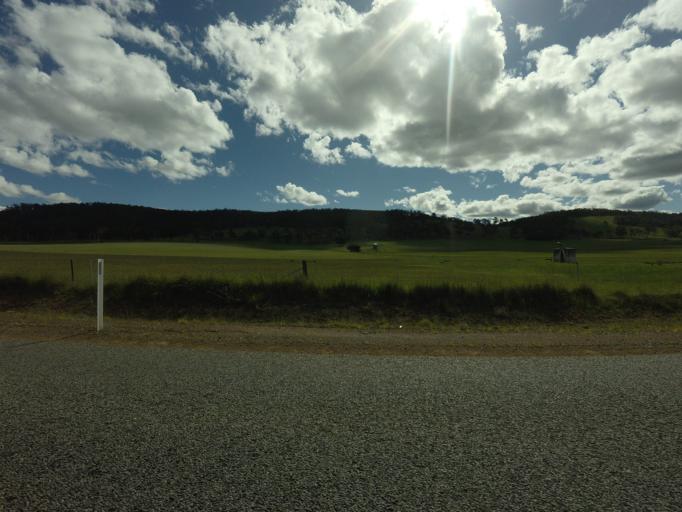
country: AU
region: Tasmania
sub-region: Brighton
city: Bridgewater
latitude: -42.4342
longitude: 147.3125
